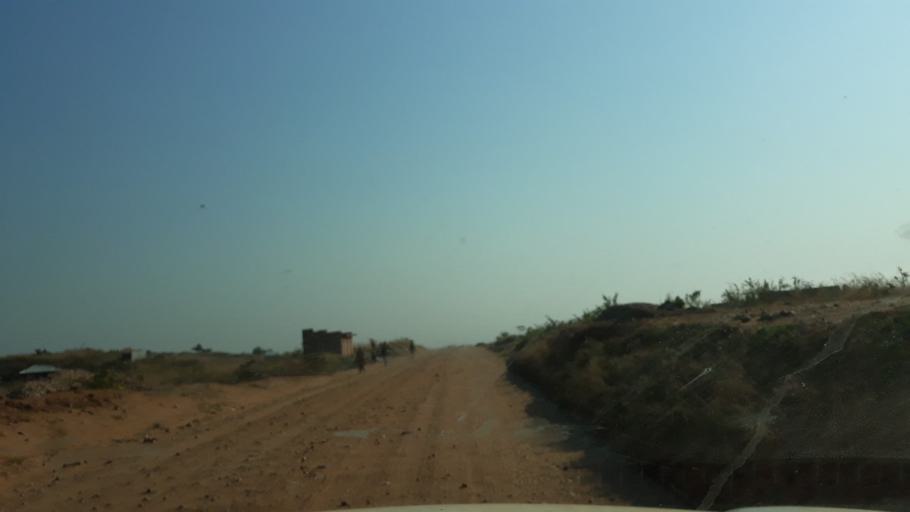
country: CD
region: Katanga
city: Kalemie
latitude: -5.8823
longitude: 29.1923
